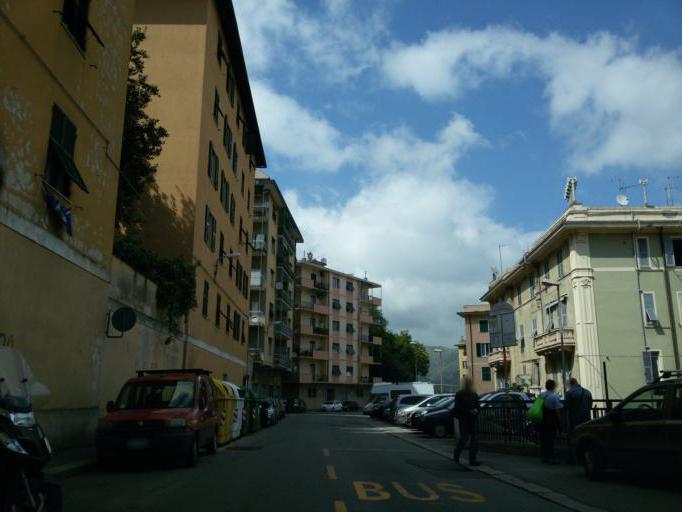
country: IT
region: Liguria
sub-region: Provincia di Genova
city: Genoa
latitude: 44.4177
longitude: 8.9461
